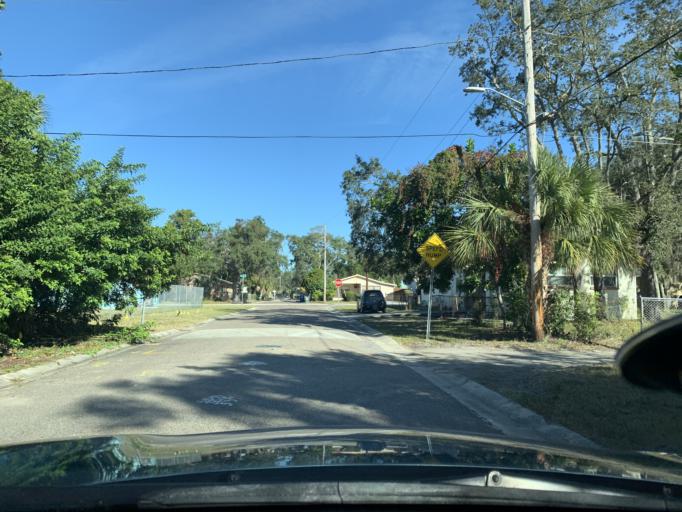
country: US
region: Florida
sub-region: Pinellas County
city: Gulfport
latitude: 27.7541
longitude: -82.6977
